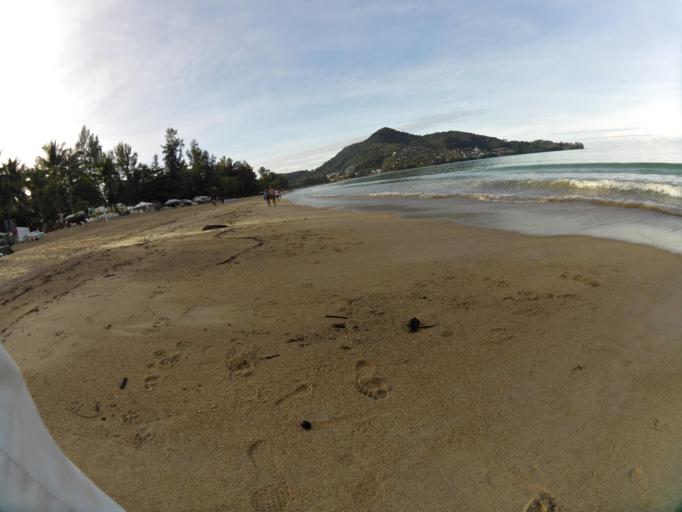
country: TH
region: Phuket
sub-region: Amphoe Kathu
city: Kathu
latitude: 7.9599
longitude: 98.2836
